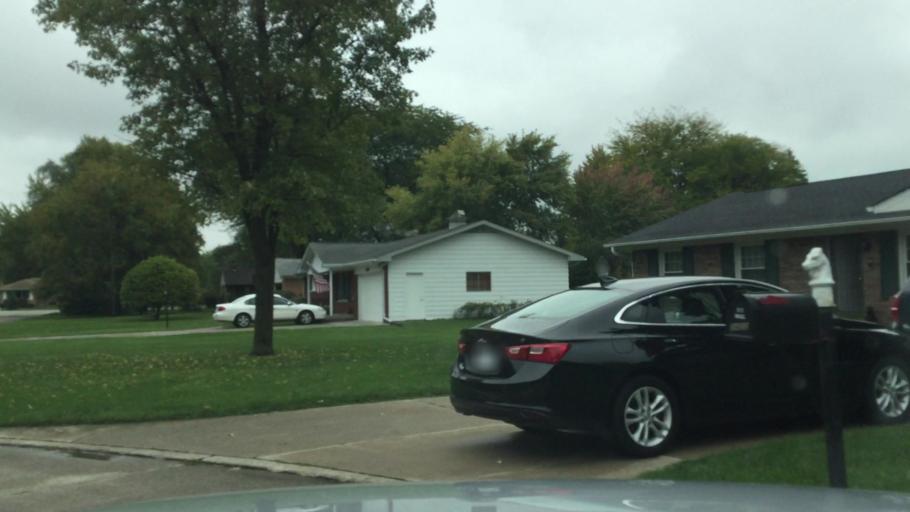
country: US
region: Michigan
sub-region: Saginaw County
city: Shields
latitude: 43.4426
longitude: -84.0061
